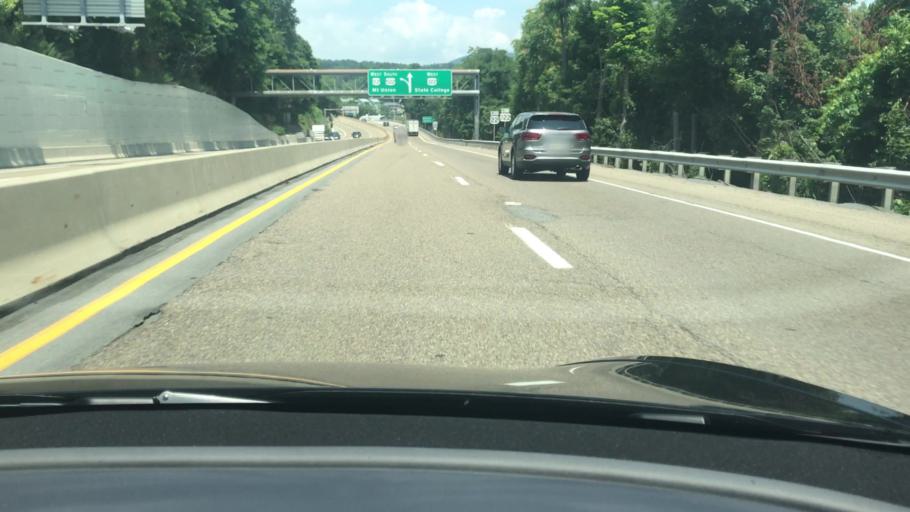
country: US
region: Pennsylvania
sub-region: Mifflin County
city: Lewistown
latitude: 40.6089
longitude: -77.5679
